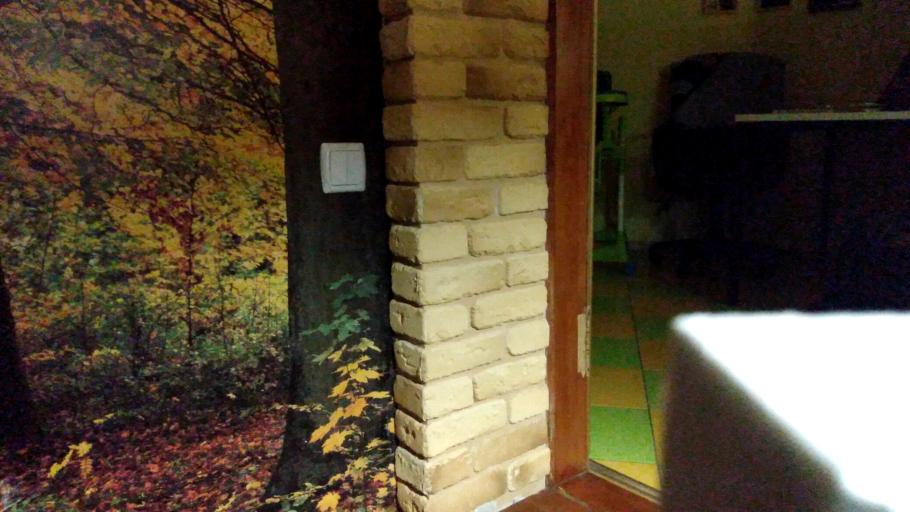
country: RU
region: Arkhangelskaya
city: Kargopol'
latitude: 61.4271
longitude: 37.8065
